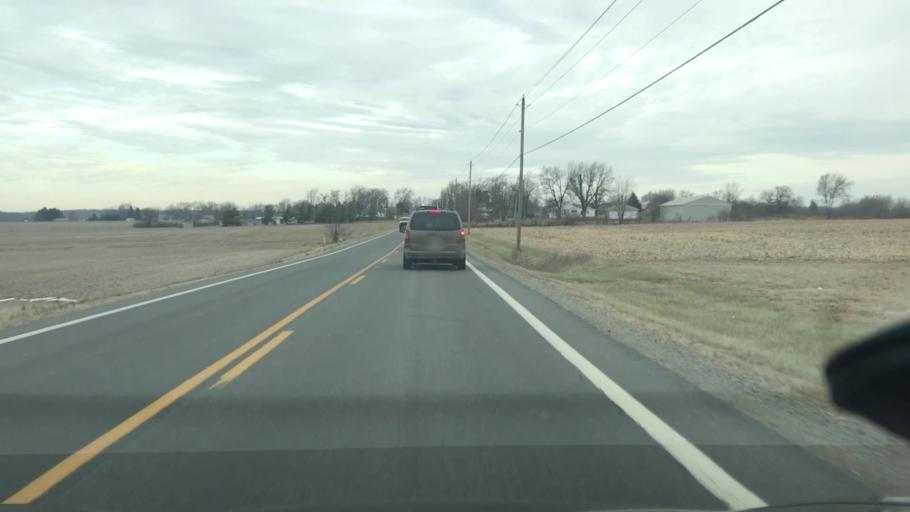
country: US
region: Ohio
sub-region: Madison County
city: Choctaw Lake
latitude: 39.9270
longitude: -83.4880
